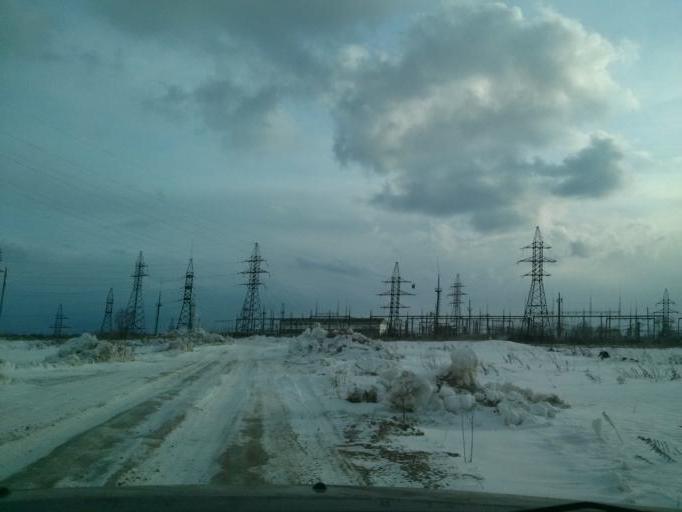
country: RU
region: Nizjnij Novgorod
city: Afonino
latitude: 56.2669
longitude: 44.0311
